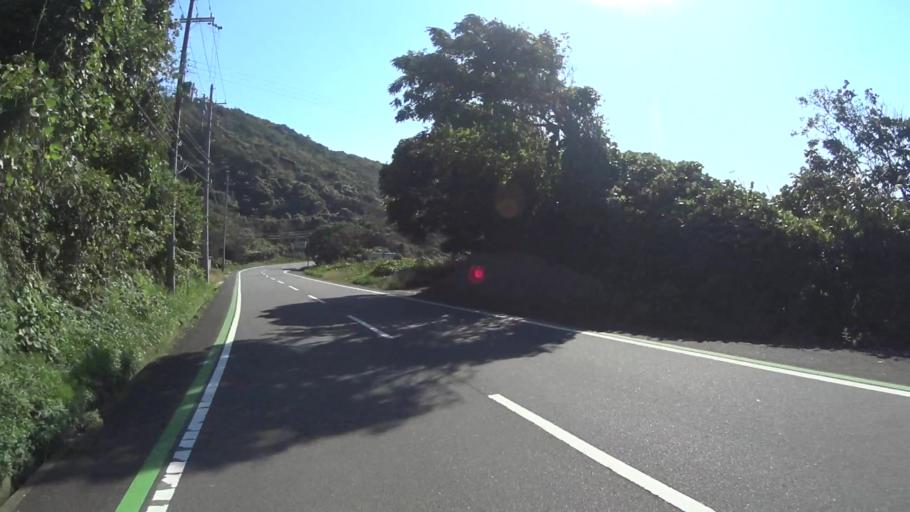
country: JP
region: Kyoto
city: Miyazu
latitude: 35.7260
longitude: 135.0859
